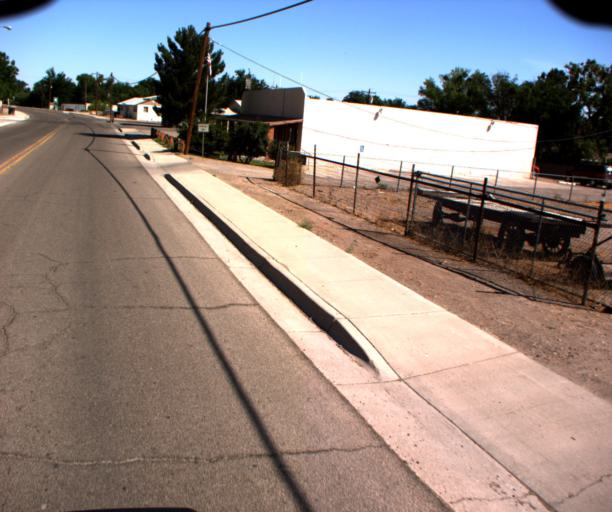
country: US
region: Arizona
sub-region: Greenlee County
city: Clifton
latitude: 32.7148
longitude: -109.1003
